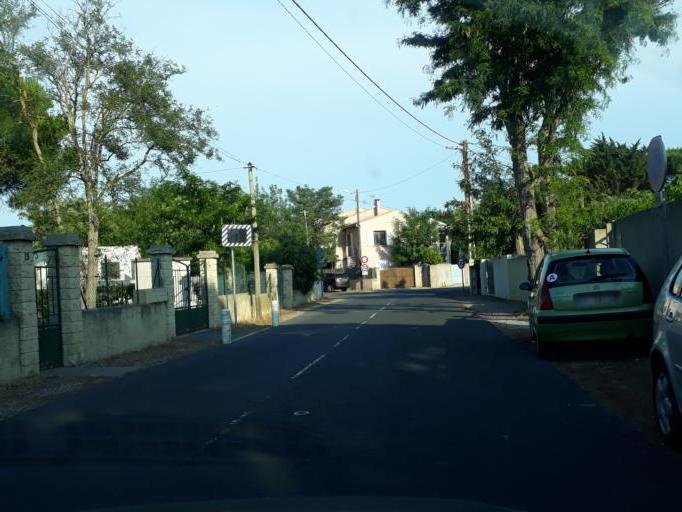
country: FR
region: Languedoc-Roussillon
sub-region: Departement de l'Herault
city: Agde
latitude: 43.2835
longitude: 3.4551
